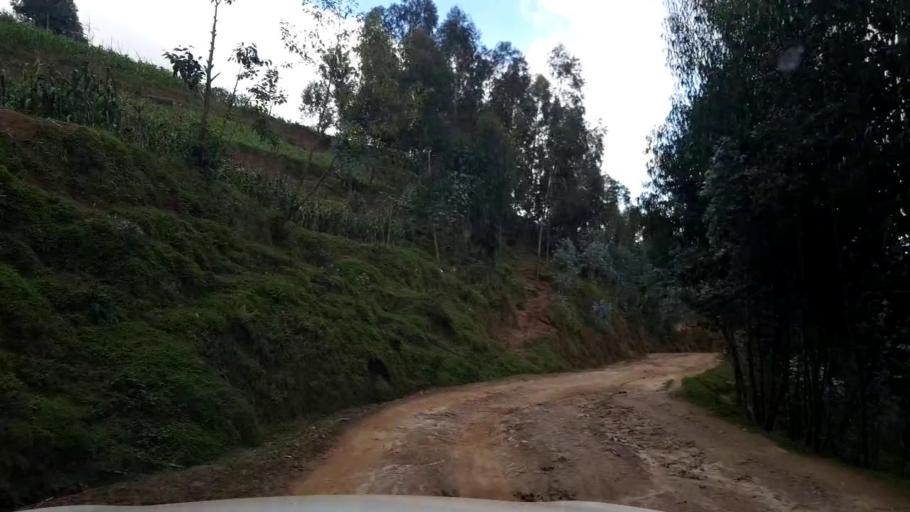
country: RW
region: Western Province
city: Kibuye
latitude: -1.8921
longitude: 29.4641
